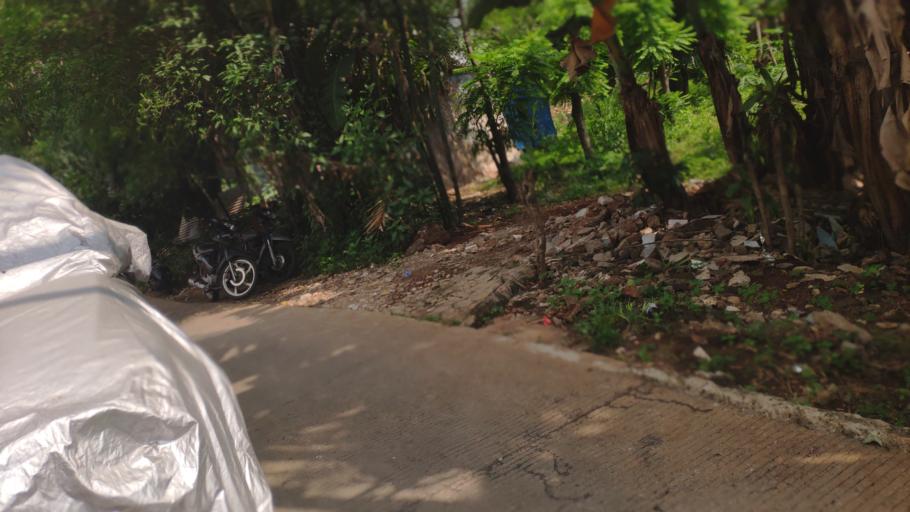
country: ID
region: Jakarta Raya
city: Jakarta
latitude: -6.2612
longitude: 106.8273
